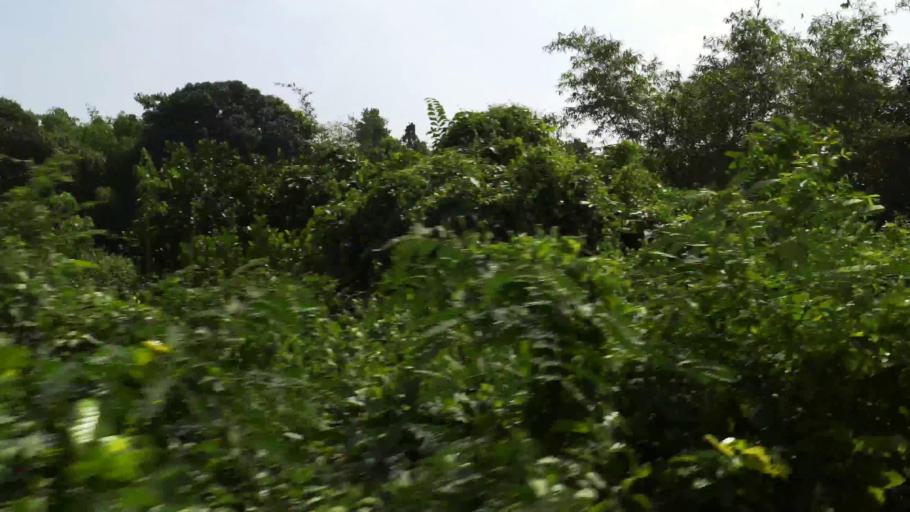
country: BD
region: Dhaka
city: Tungi
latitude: 24.1562
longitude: 90.4667
